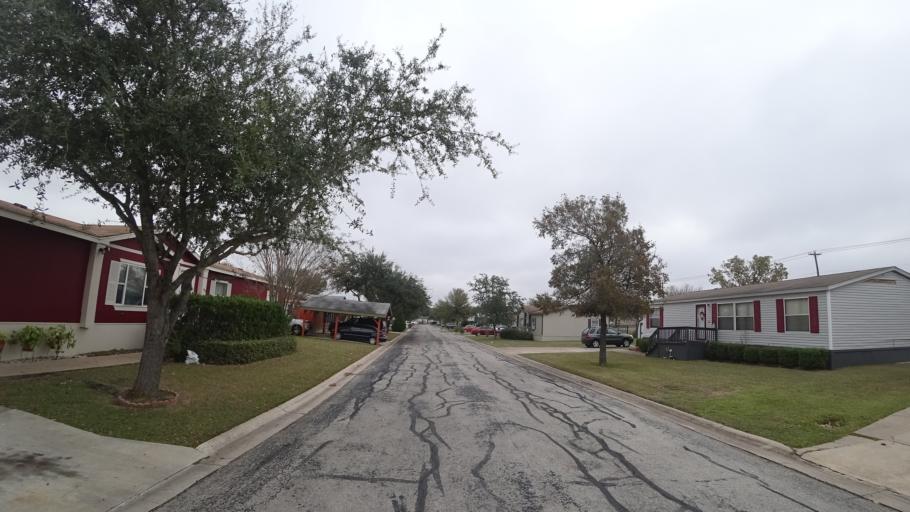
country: US
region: Texas
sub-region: Travis County
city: Pflugerville
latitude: 30.4137
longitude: -97.6081
